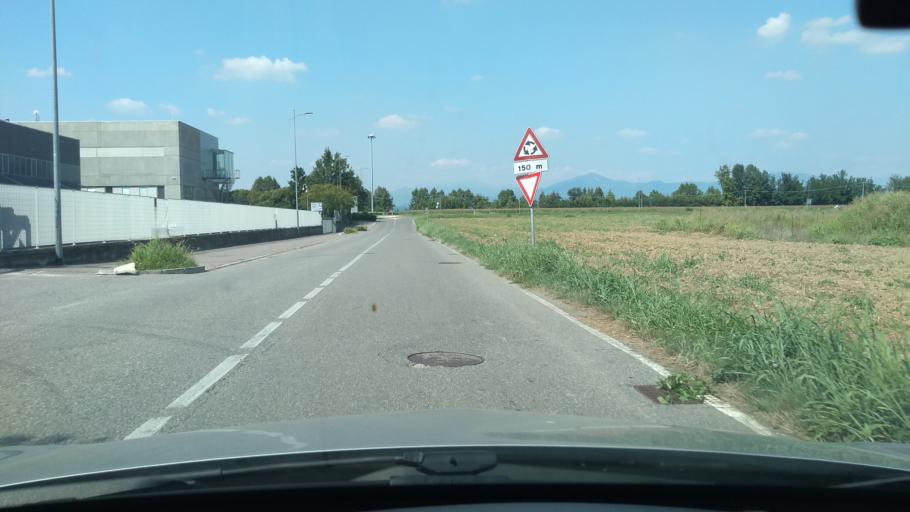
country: IT
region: Lombardy
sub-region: Provincia di Bergamo
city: Mornico al Serio
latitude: 45.5938
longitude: 9.7876
